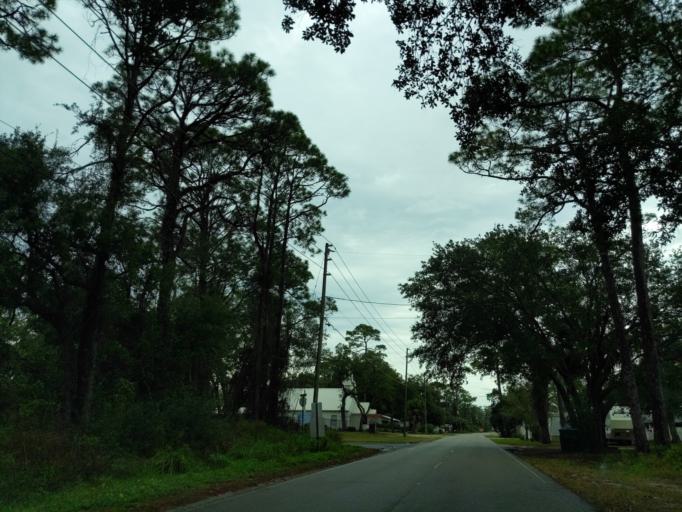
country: US
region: Florida
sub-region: Franklin County
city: Eastpoint
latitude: 29.7344
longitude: -84.8826
